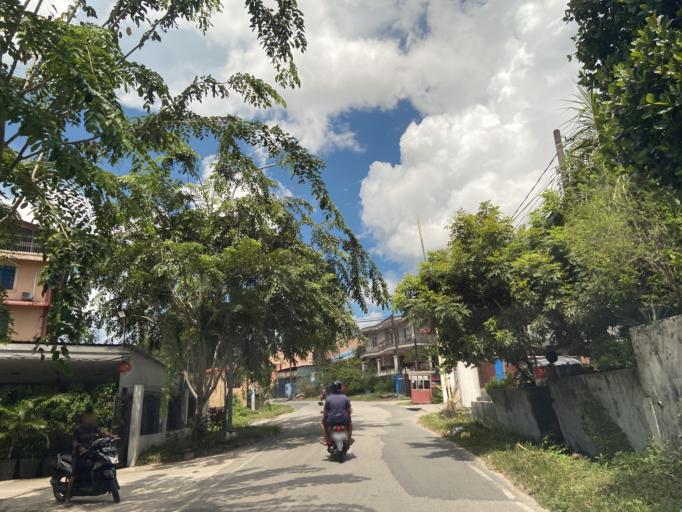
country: SG
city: Singapore
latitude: 1.1362
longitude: 104.0141
